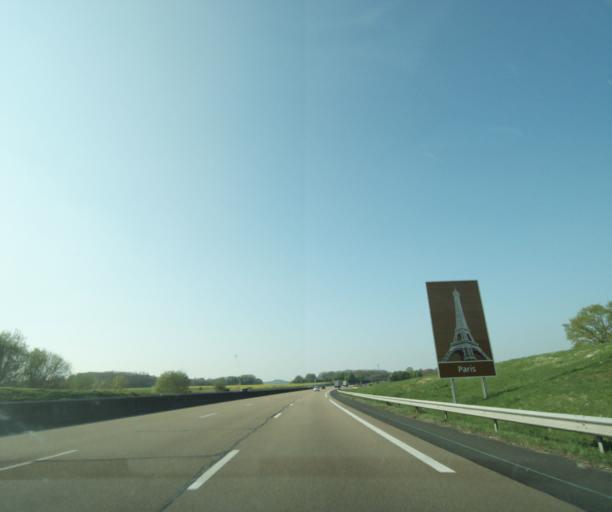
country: FR
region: Ile-de-France
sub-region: Departement de Seine-et-Marne
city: Cely
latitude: 48.4578
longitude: 2.5199
